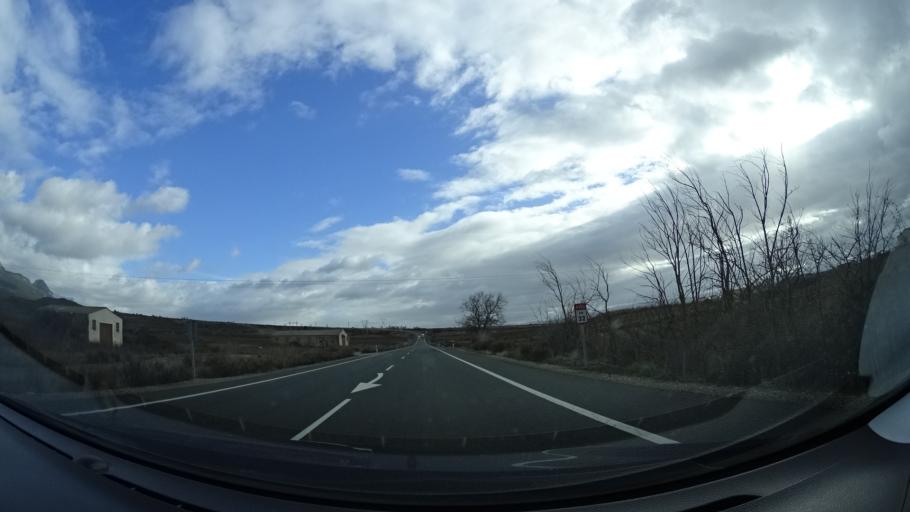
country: ES
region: La Rioja
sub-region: Provincia de La Rioja
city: San Vicente de la Sonsierra
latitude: 42.5701
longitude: -2.7518
